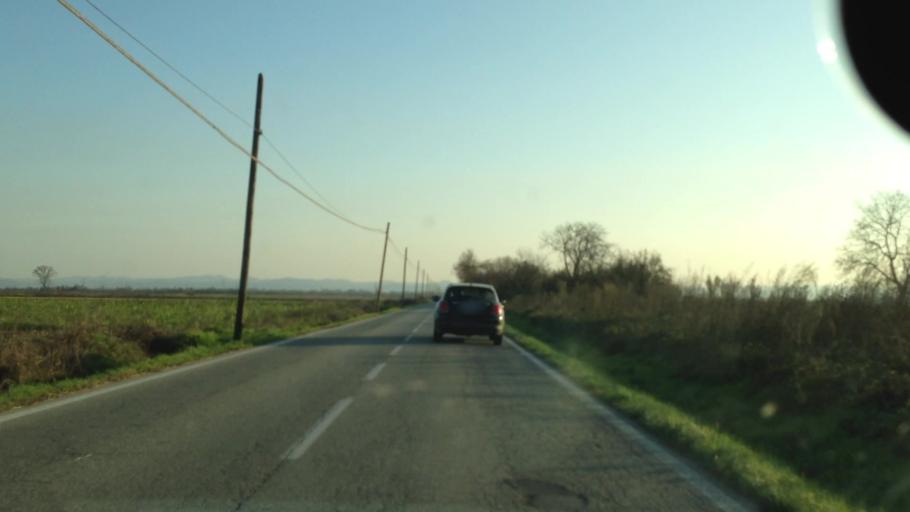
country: IT
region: Piedmont
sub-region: Provincia di Vercelli
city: Livorno Ferraris
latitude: 45.2672
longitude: 8.0827
